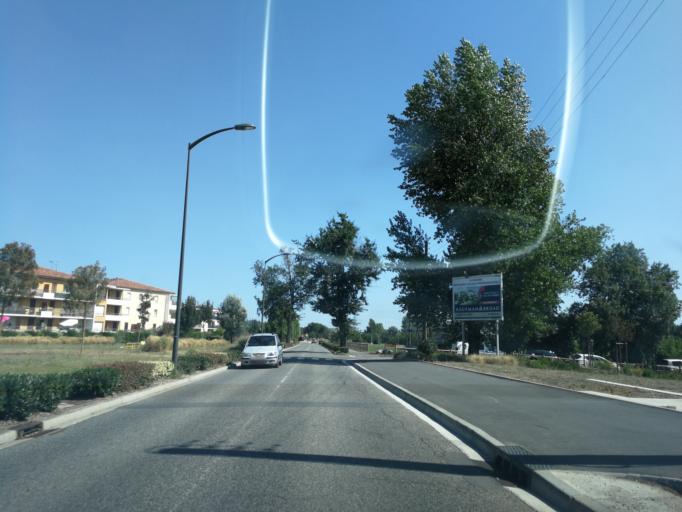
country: FR
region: Midi-Pyrenees
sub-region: Departement de la Haute-Garonne
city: Saint-Orens-de-Gameville
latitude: 43.5807
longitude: 1.5366
